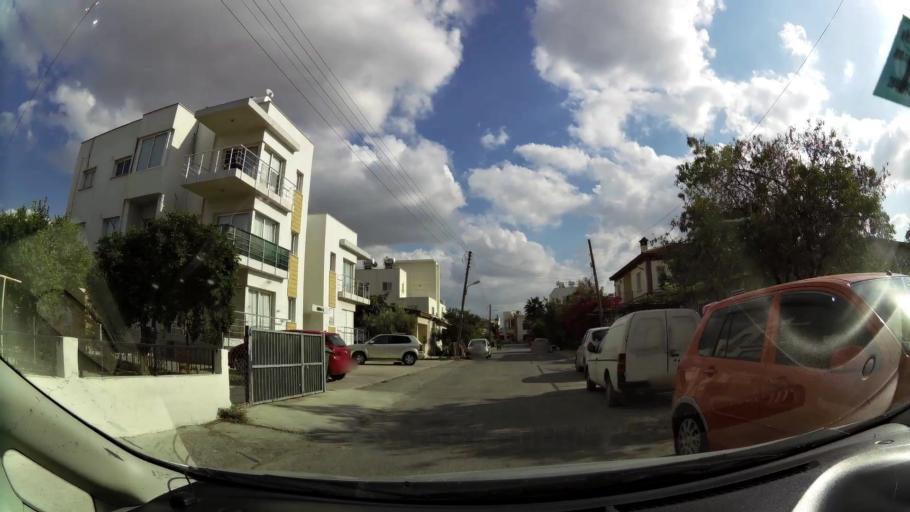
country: CY
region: Lefkosia
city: Nicosia
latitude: 35.2006
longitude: 33.3522
